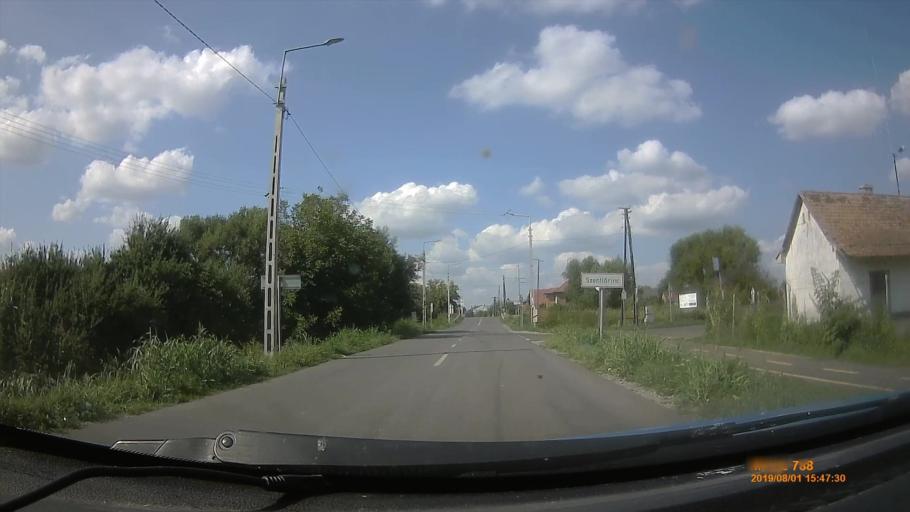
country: HU
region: Baranya
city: Szentlorinc
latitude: 46.0324
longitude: 17.9847
